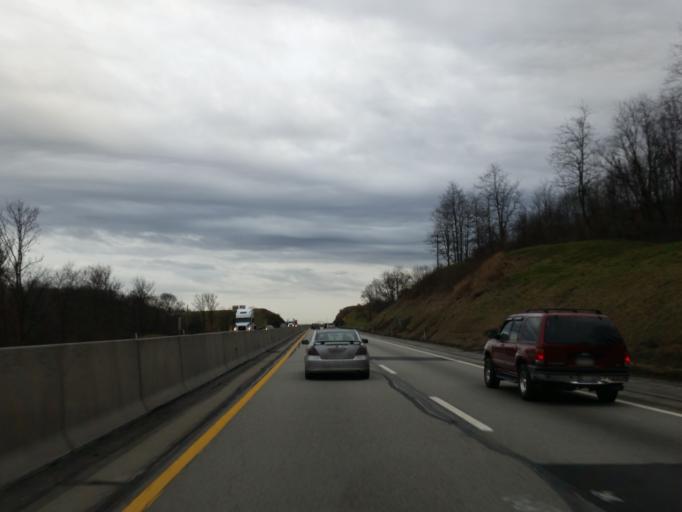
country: US
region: Pennsylvania
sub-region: Somerset County
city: Somerset
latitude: 40.0504
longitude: -79.1246
